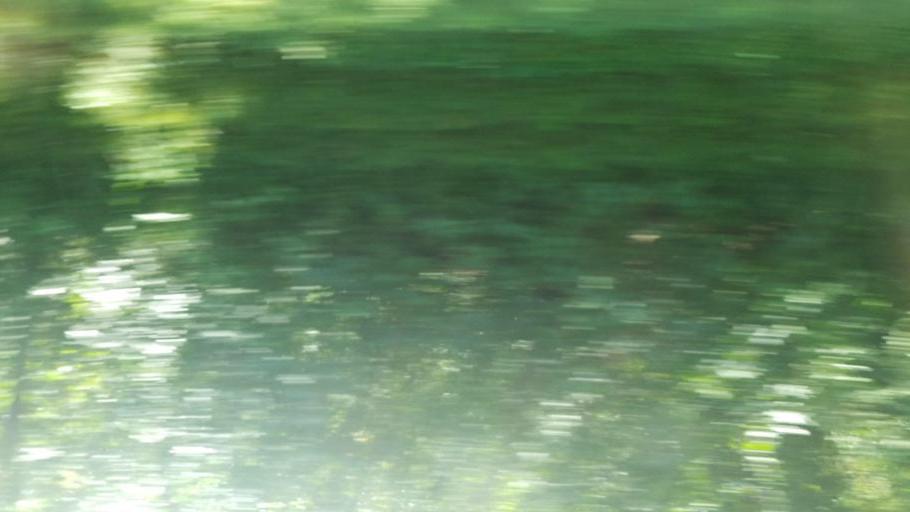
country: US
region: Illinois
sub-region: Williamson County
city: Johnston City
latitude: 37.7894
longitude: -88.8932
